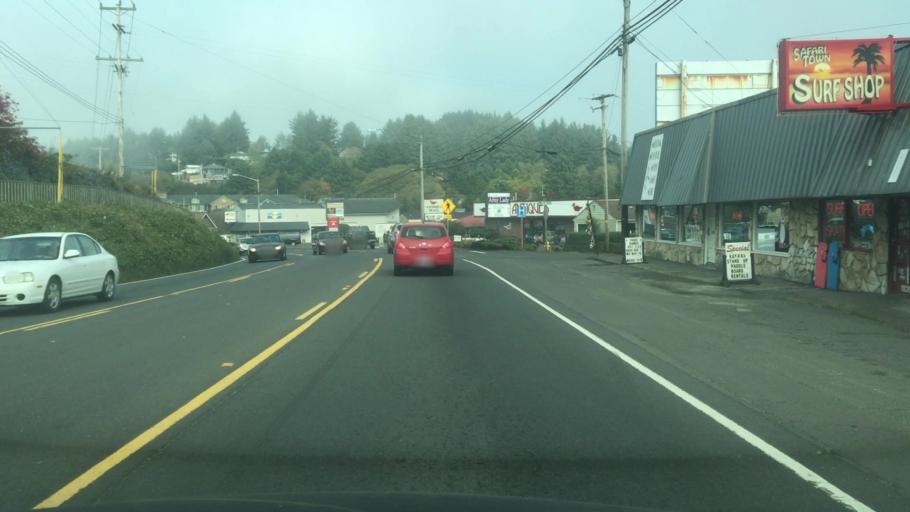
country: US
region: Oregon
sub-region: Lincoln County
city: Lincoln City
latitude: 44.9874
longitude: -124.0058
